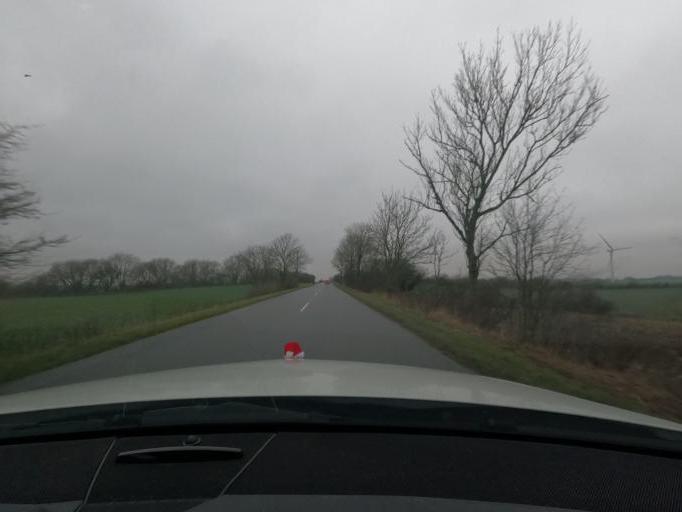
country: DK
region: South Denmark
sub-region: Haderslev Kommune
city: Haderslev
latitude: 55.1962
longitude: 9.4652
